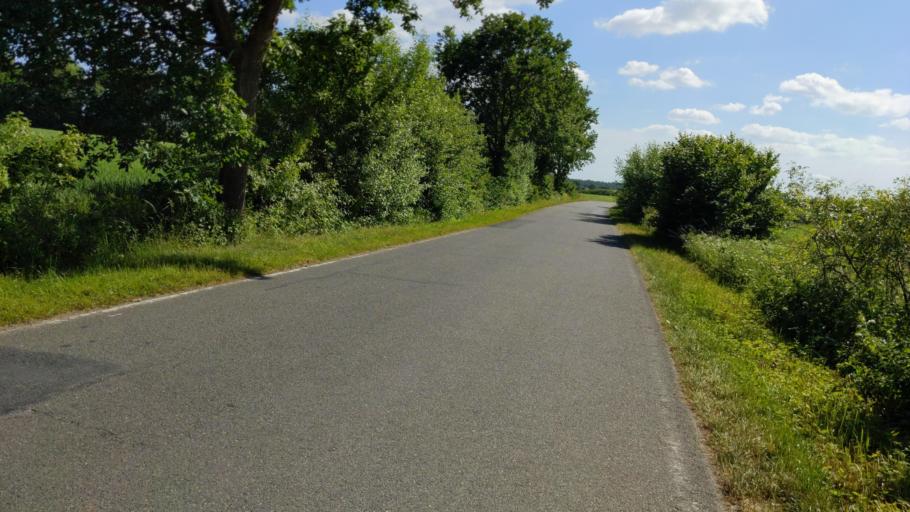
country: DE
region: Schleswig-Holstein
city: Harmsdorf
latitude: 53.6949
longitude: 10.7206
